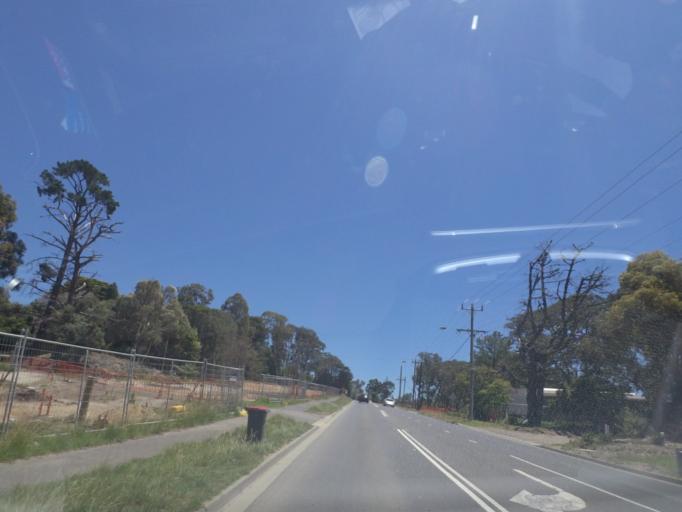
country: AU
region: Victoria
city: Plenty
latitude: -37.6654
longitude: 145.1241
